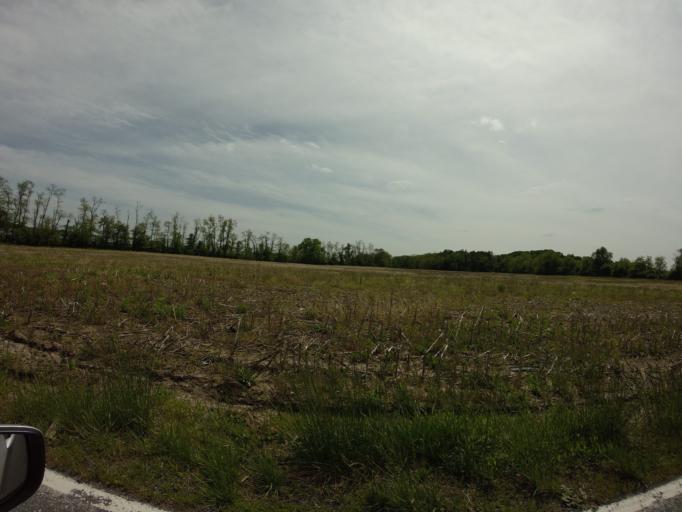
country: US
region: Maryland
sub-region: Frederick County
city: Linganore
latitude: 39.5144
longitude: -77.2221
